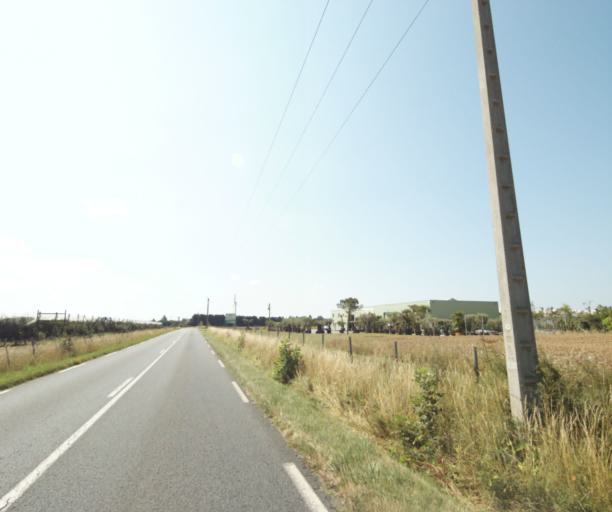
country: FR
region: Centre
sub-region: Departement du Loiret
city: Saint-Cyr-en-Val
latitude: 47.8470
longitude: 1.9569
